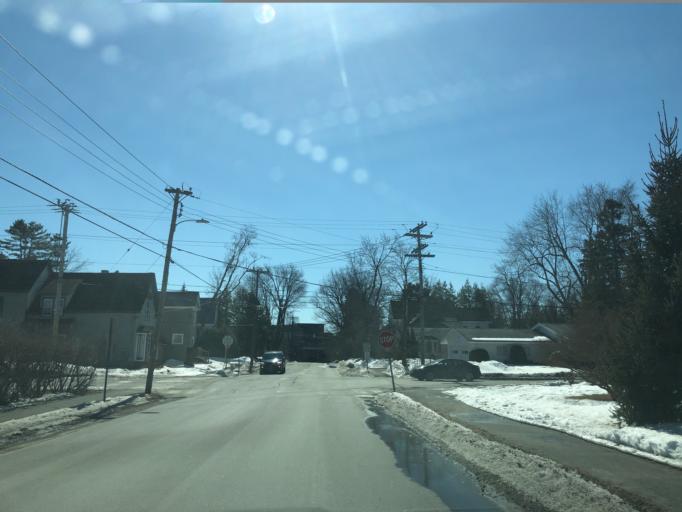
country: US
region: Maine
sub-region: Penobscot County
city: Brewer
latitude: 44.8114
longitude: -68.7525
